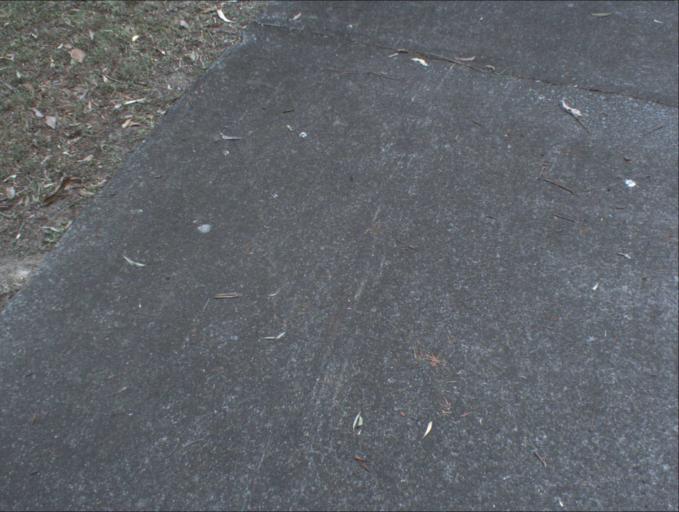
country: AU
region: Queensland
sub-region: Logan
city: Slacks Creek
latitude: -27.6543
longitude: 153.1917
